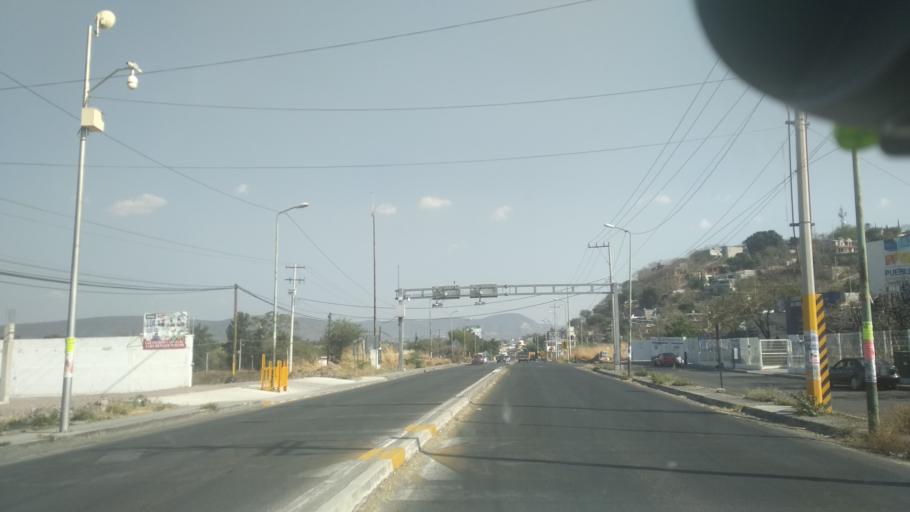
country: MX
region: Puebla
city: Izucar de Matamoros
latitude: 18.6170
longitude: -98.4688
